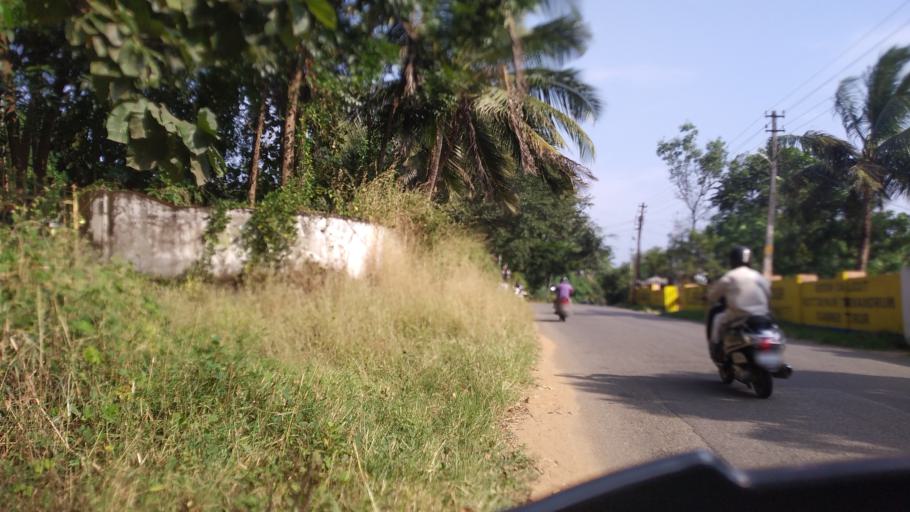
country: IN
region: Kerala
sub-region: Palakkad district
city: Palakkad
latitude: 10.5964
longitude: 76.5523
